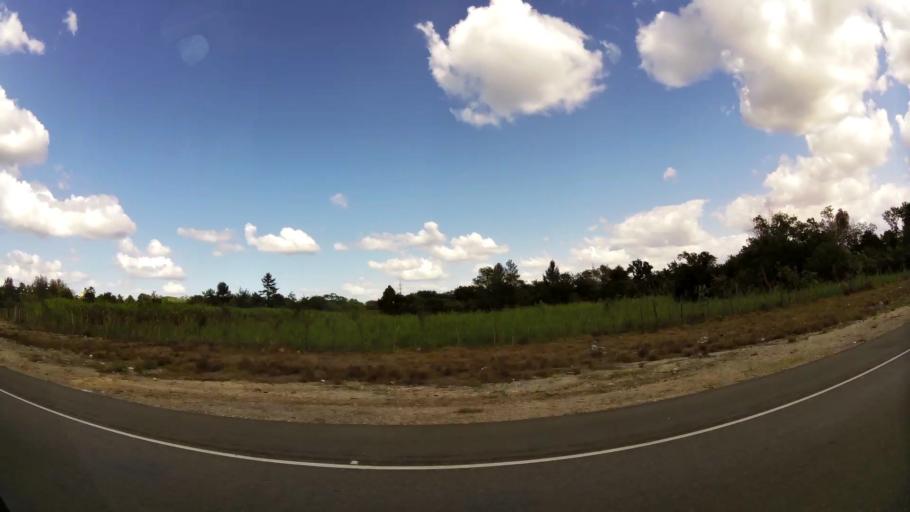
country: DO
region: Santo Domingo
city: Santo Domingo Oeste
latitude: 18.5426
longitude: -70.0790
